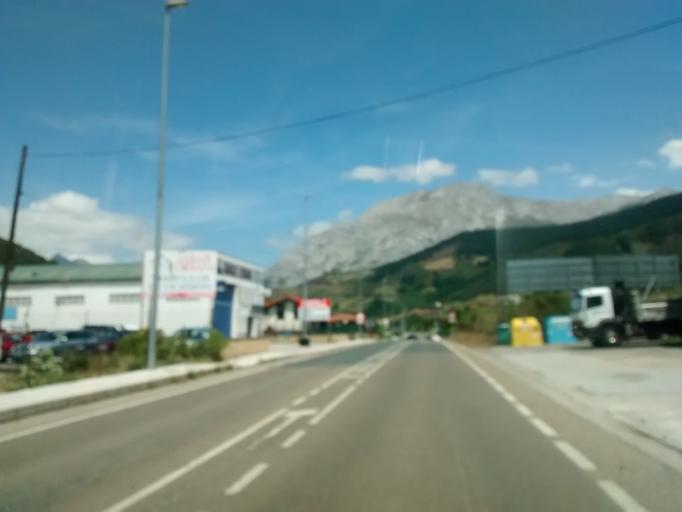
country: ES
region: Cantabria
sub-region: Provincia de Cantabria
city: Potes
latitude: 43.1651
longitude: -4.6080
